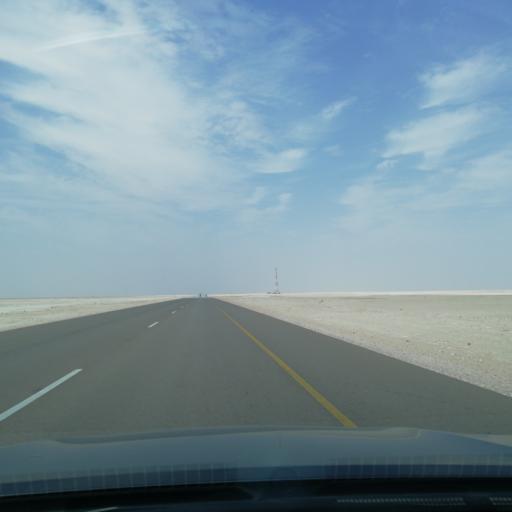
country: OM
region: Al Wusta
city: Hayma'
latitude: 20.2329
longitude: 56.5674
